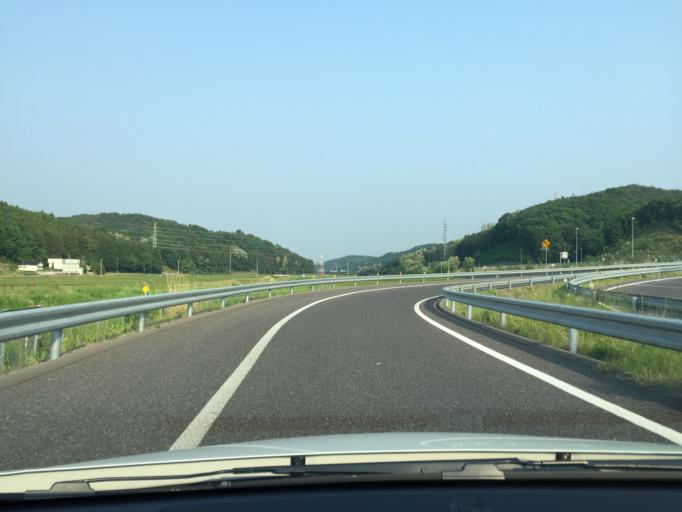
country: JP
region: Fukushima
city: Sukagawa
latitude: 37.1484
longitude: 140.2200
